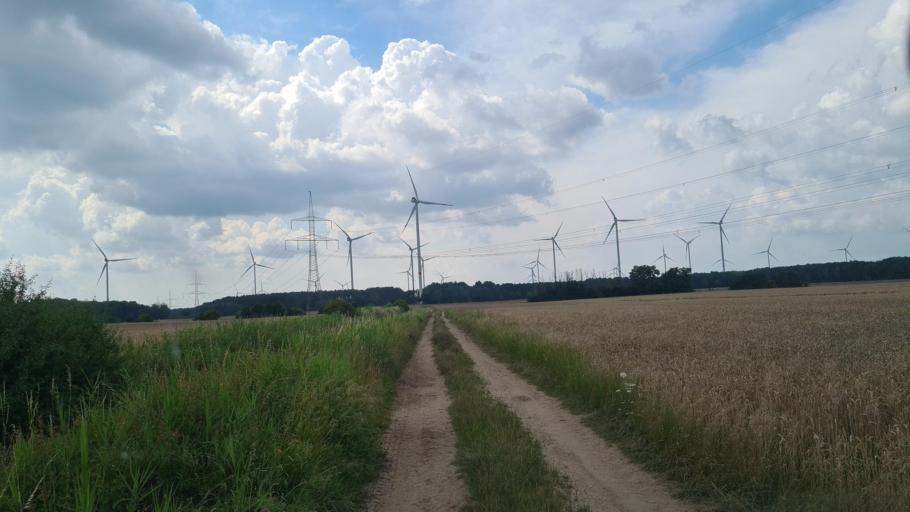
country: DE
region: Brandenburg
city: Sallgast
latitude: 51.6270
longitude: 13.8516
